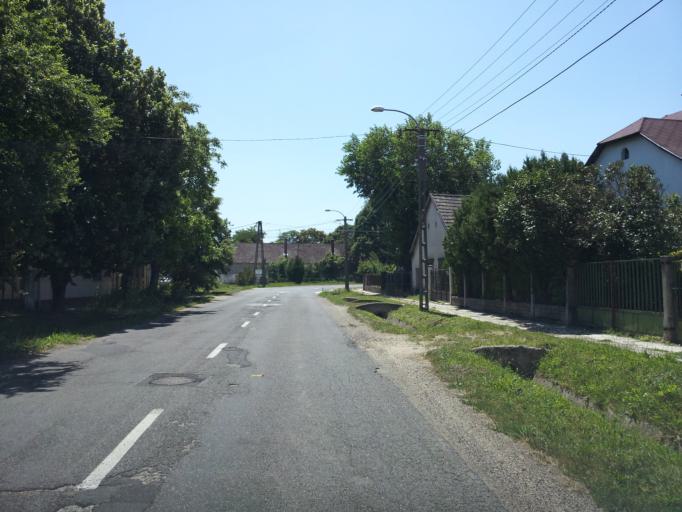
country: HU
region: Veszprem
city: Berhida
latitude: 47.1145
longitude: 18.1366
